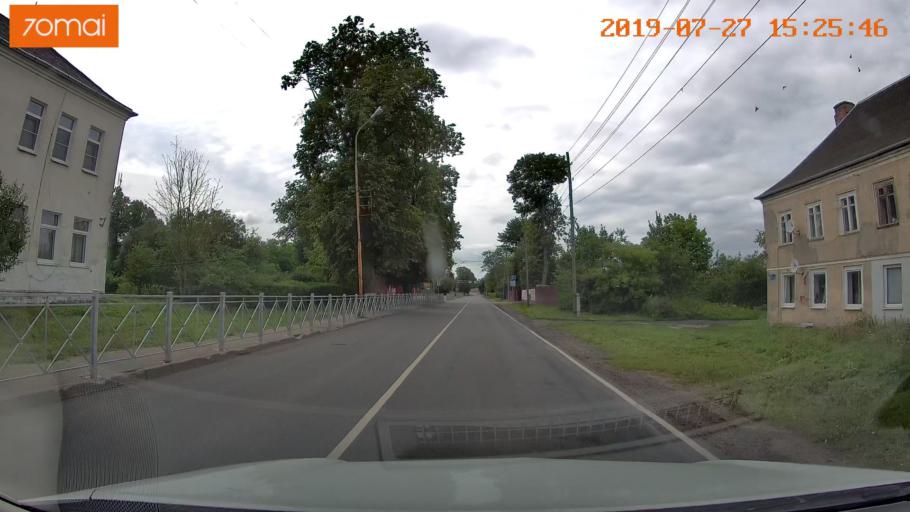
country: RU
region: Kaliningrad
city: Nesterov
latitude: 54.6312
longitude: 22.5834
